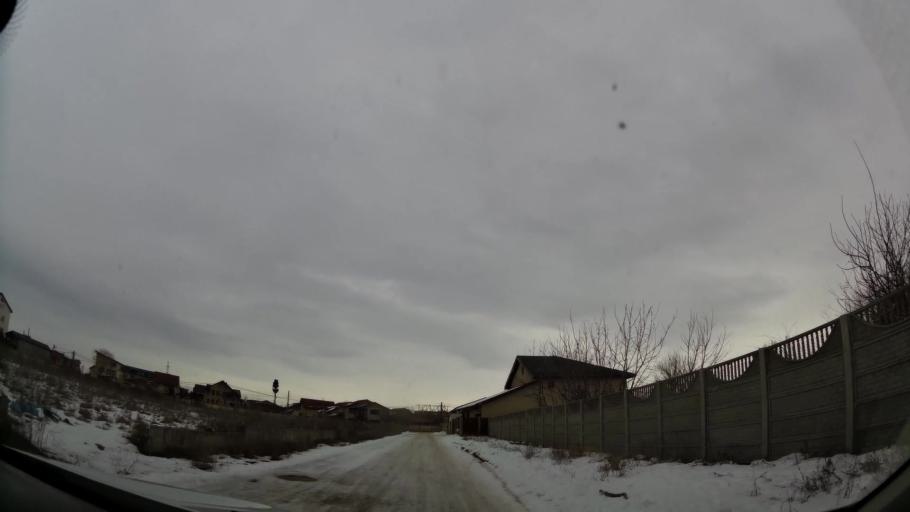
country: RO
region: Ilfov
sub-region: Comuna Pantelimon
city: Pantelimon
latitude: 44.4546
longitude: 26.2186
